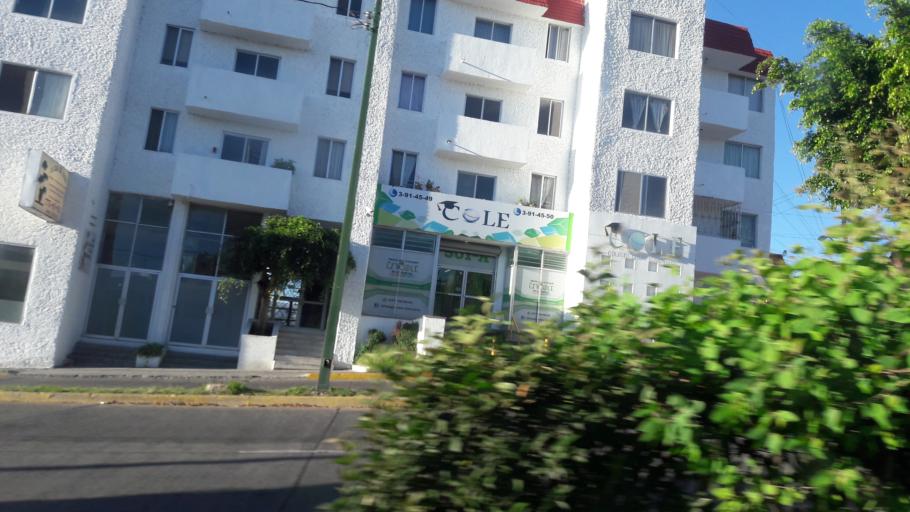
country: MX
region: Guanajuato
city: Leon
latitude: 21.1437
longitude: -101.6932
